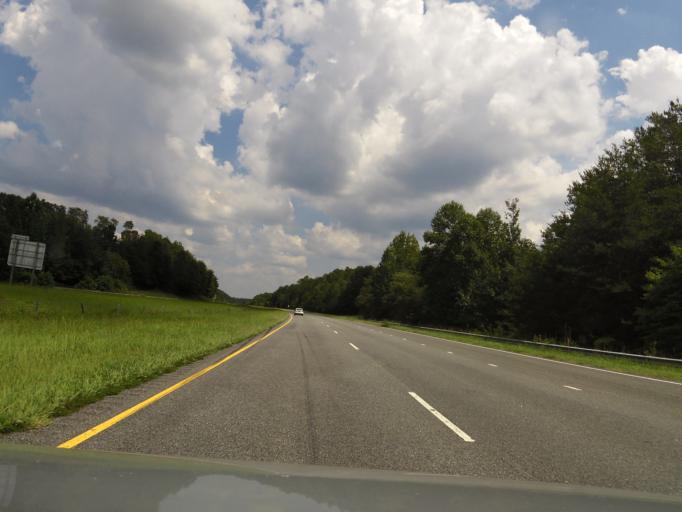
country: US
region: North Carolina
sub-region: Polk County
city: Columbus
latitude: 35.2835
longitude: -82.1092
